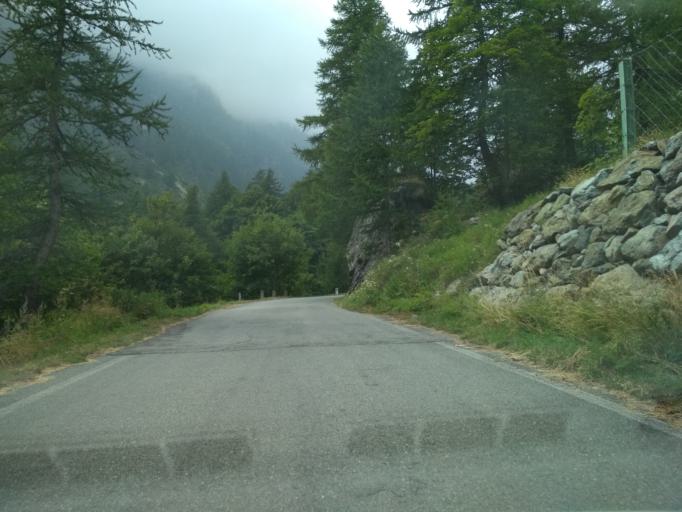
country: IT
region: Piedmont
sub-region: Provincia di Torino
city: Balme
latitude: 45.3030
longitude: 7.2077
